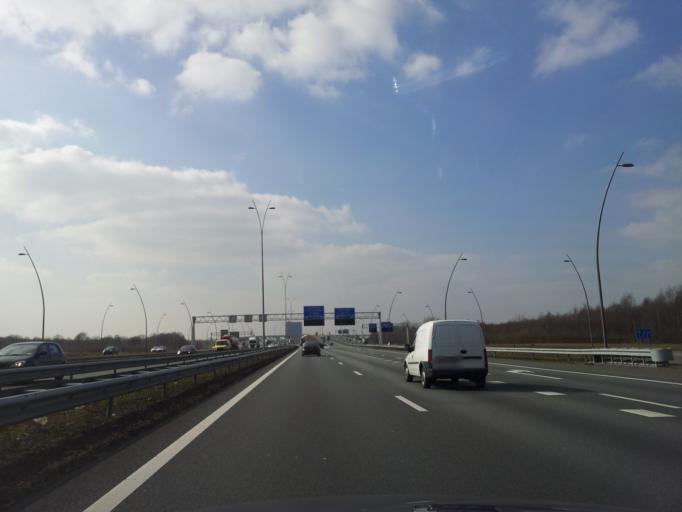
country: NL
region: North Brabant
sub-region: Gemeente Waalre
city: Waalre
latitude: 51.4054
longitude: 5.4482
